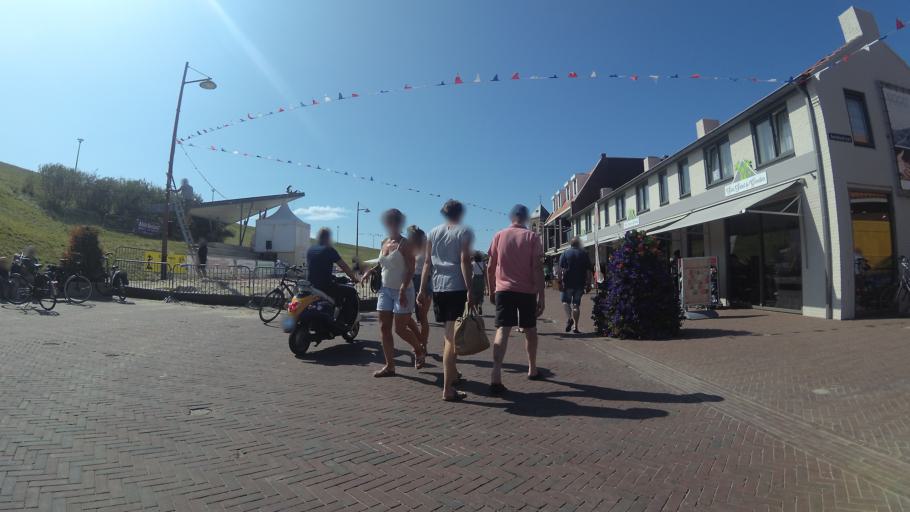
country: NL
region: Zeeland
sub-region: Gemeente Vlissingen
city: Vlissingen
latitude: 51.5002
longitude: 3.4829
